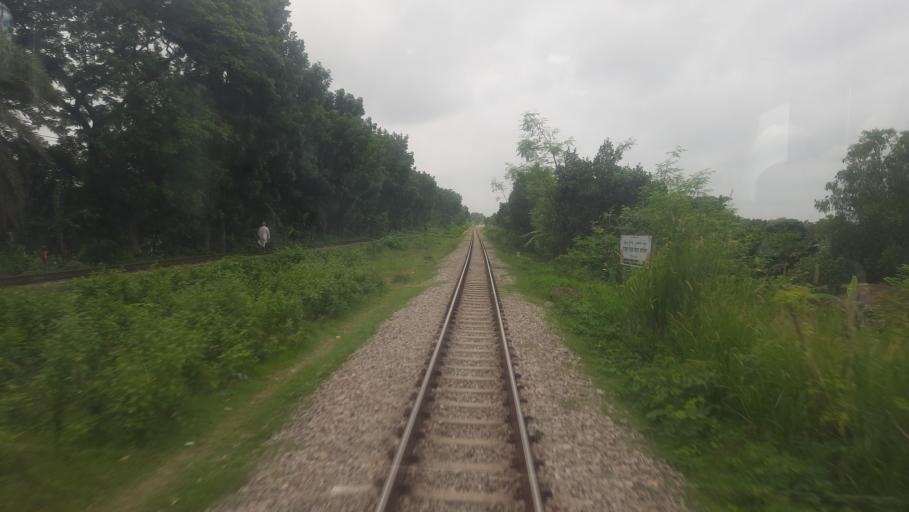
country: BD
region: Dhaka
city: Narsingdi
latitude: 23.9322
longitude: 90.7513
